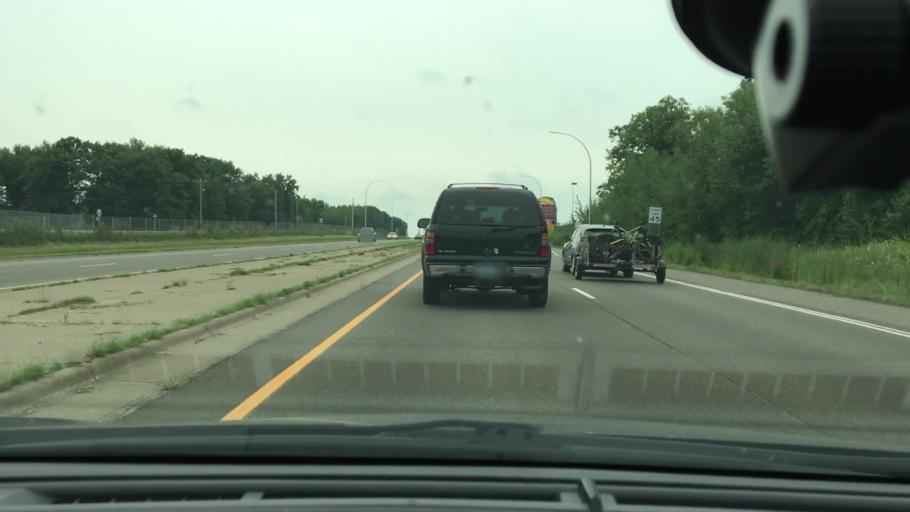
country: US
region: Minnesota
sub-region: Mille Lacs County
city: Vineland
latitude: 46.1836
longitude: -93.7566
